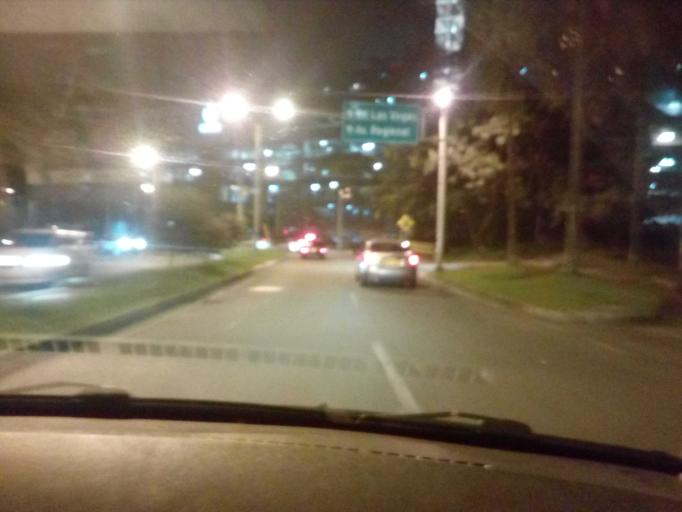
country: CO
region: Antioquia
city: Itagui
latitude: 6.1979
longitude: -75.5755
